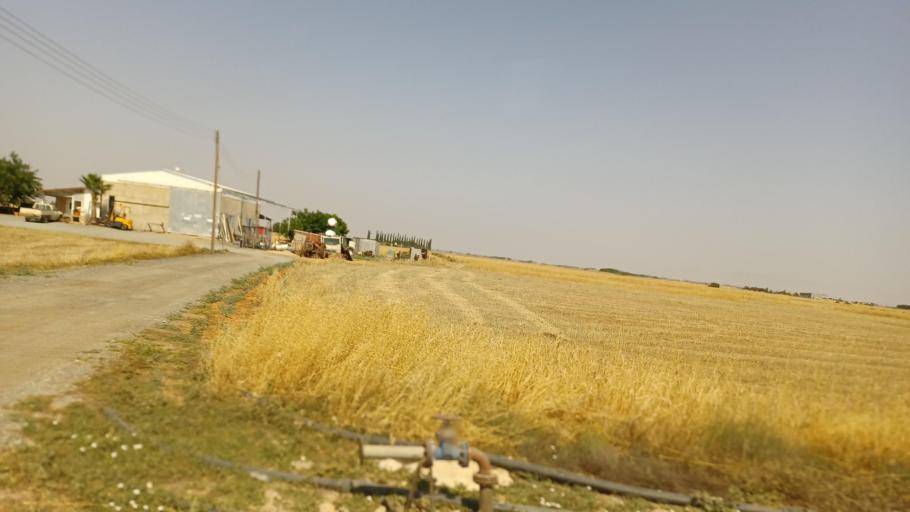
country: CY
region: Ammochostos
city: Avgorou
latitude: 35.0479
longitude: 33.8515
